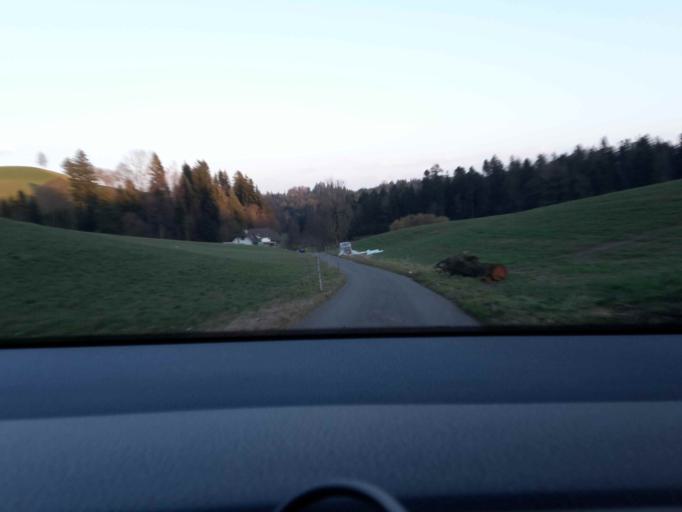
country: CH
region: Bern
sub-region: Oberaargau
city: Huttwil
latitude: 47.1267
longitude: 7.8629
